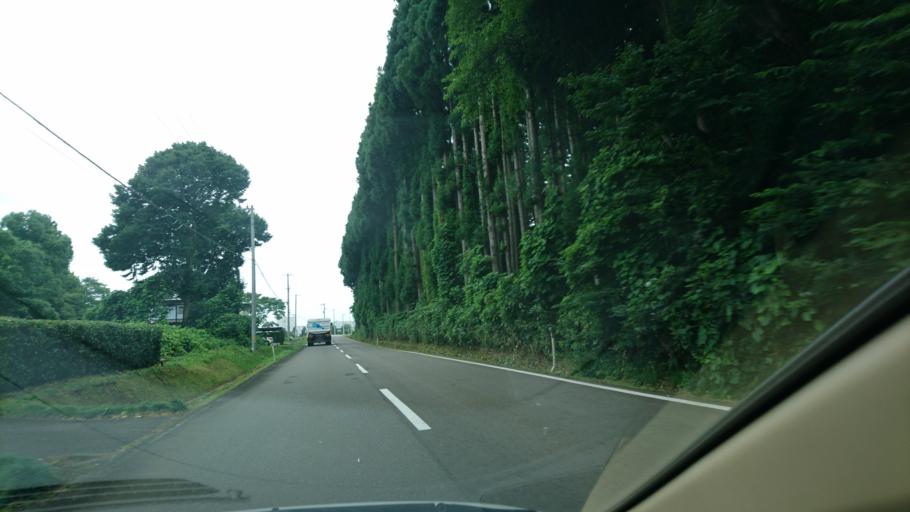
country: JP
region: Iwate
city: Kitakami
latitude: 39.2393
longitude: 141.0999
